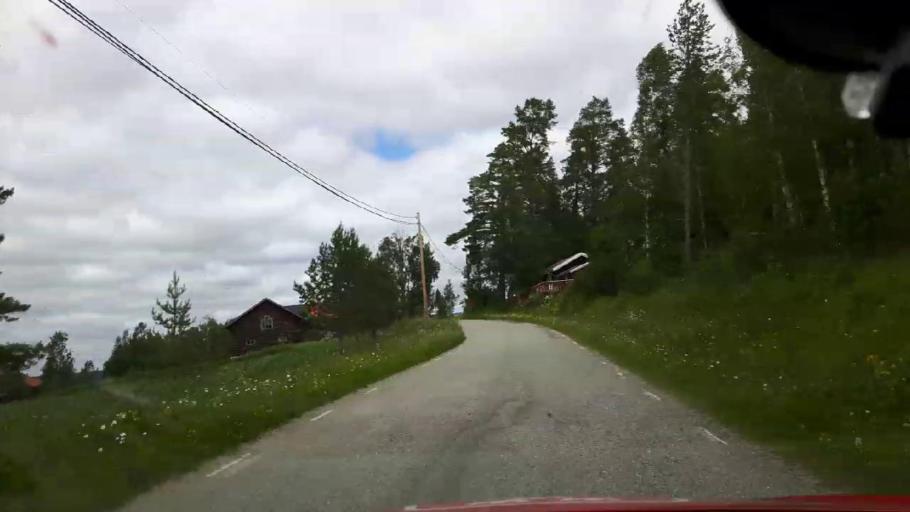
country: SE
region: Jaemtland
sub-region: Braecke Kommun
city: Braecke
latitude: 62.8661
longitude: 15.2718
